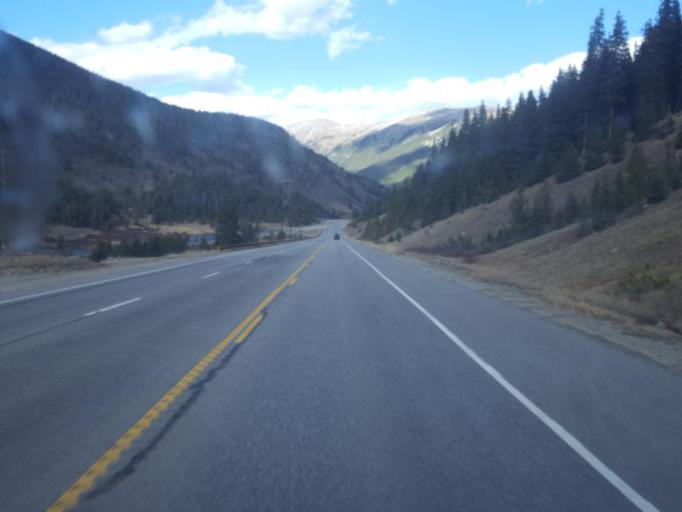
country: US
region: Colorado
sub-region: Summit County
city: Breckenridge
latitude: 39.4511
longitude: -106.1482
